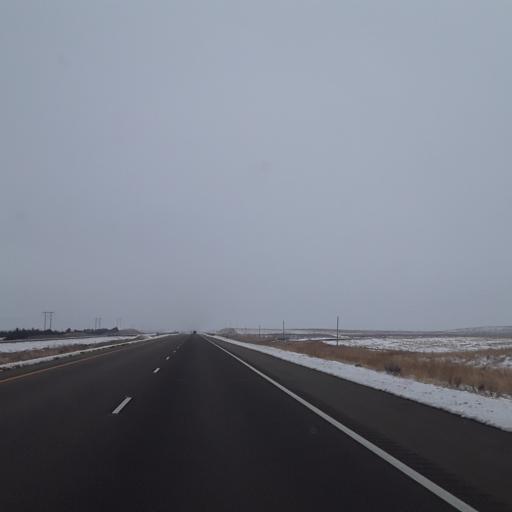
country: US
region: Colorado
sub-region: Logan County
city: Sterling
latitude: 40.4742
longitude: -103.2849
